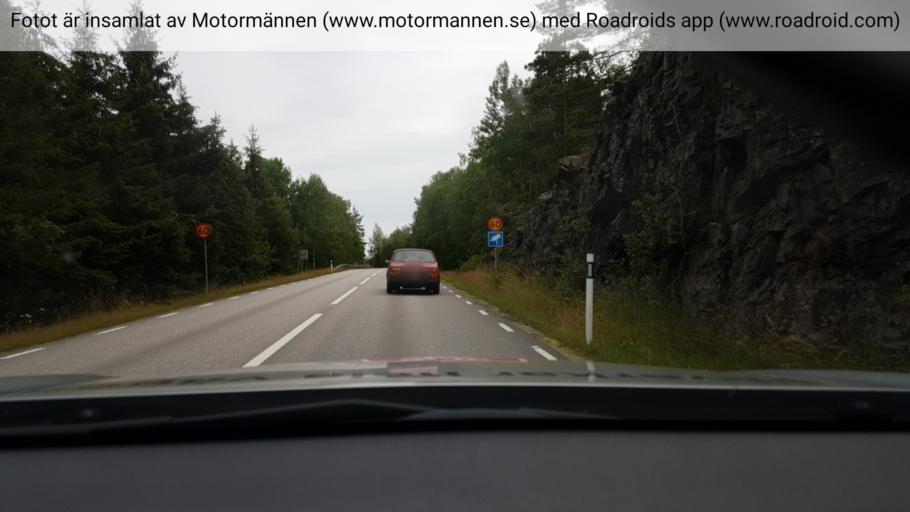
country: SE
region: Vaestra Goetaland
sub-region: Bengtsfors Kommun
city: Billingsfors
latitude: 58.9268
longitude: 12.2147
